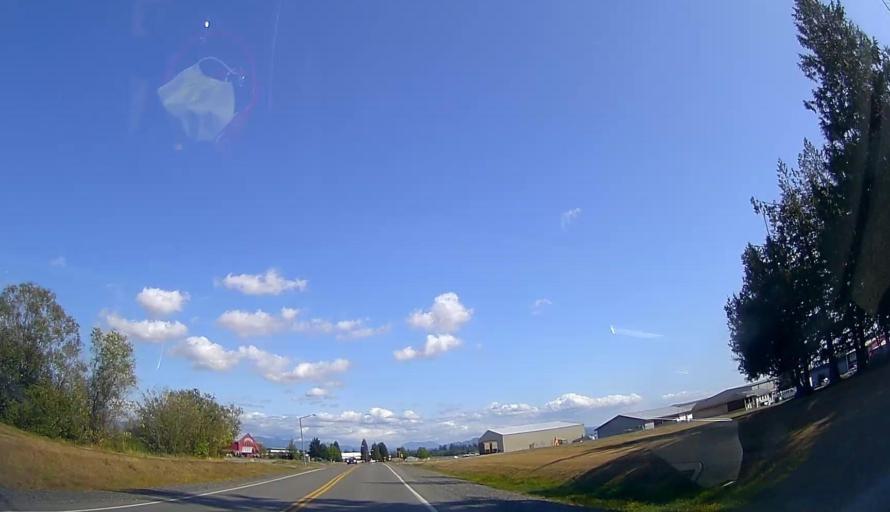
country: US
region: Washington
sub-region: Skagit County
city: Burlington
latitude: 48.4737
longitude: -122.4141
